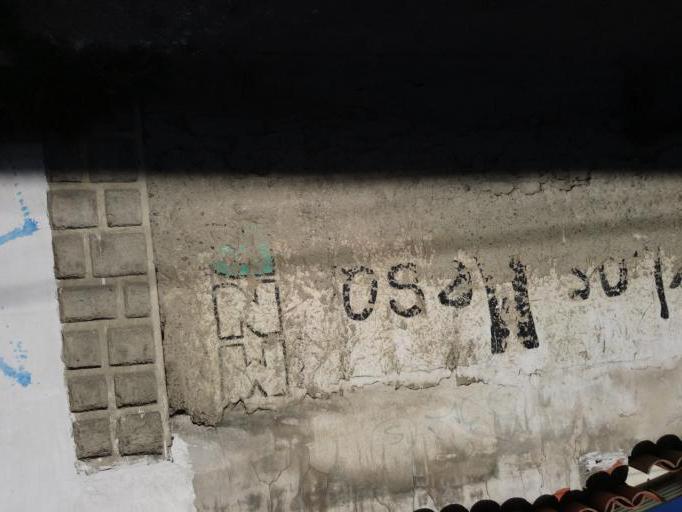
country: BO
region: La Paz
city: La Paz
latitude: -16.5107
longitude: -68.1137
